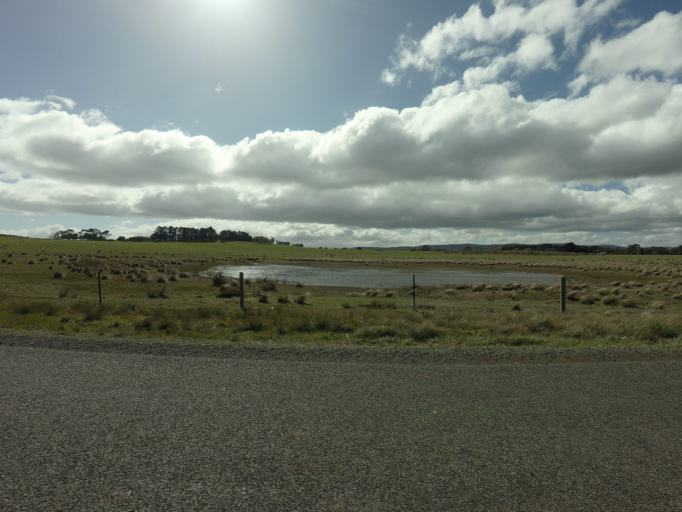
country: AU
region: Tasmania
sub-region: Northern Midlands
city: Evandale
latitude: -41.9186
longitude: 147.4772
